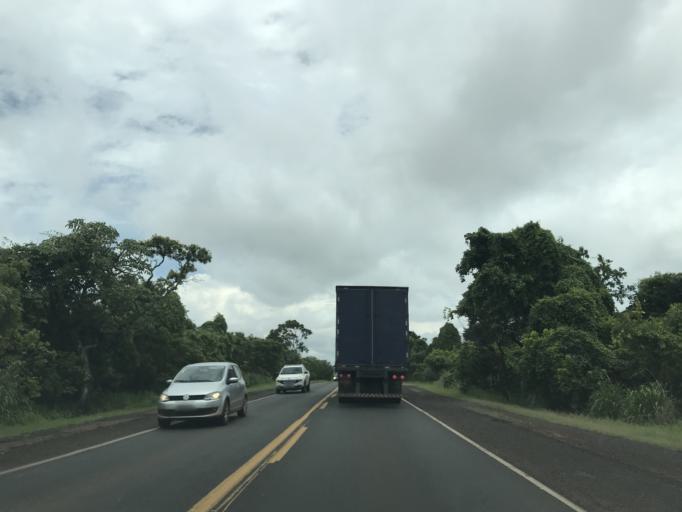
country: BR
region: Minas Gerais
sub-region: Frutal
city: Frutal
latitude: -19.7750
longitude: -48.9653
